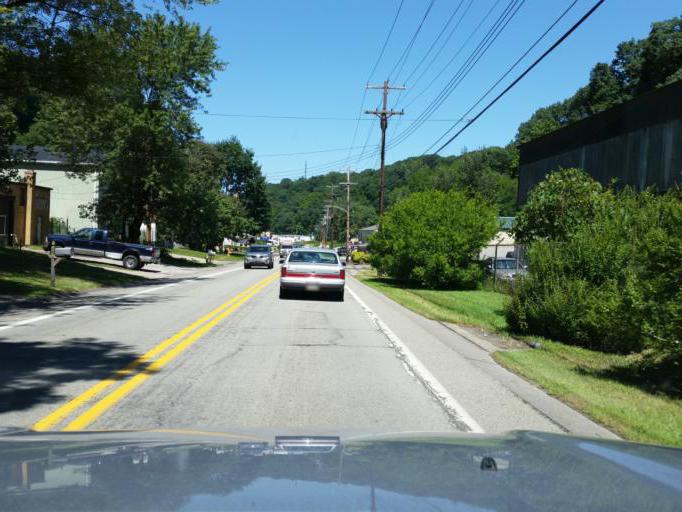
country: US
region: Pennsylvania
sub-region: Allegheny County
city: Blawnox
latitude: 40.4795
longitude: -79.8487
